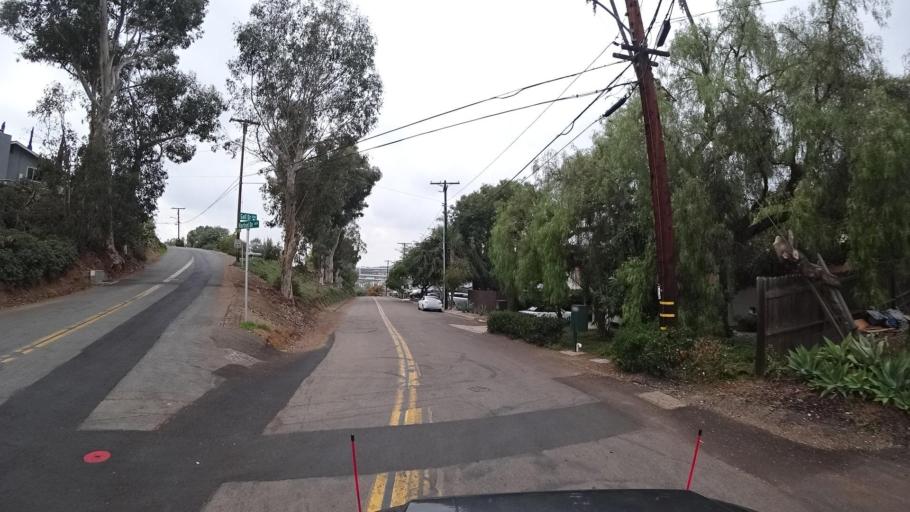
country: US
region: California
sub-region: San Diego County
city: Spring Valley
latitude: 32.7476
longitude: -117.0088
